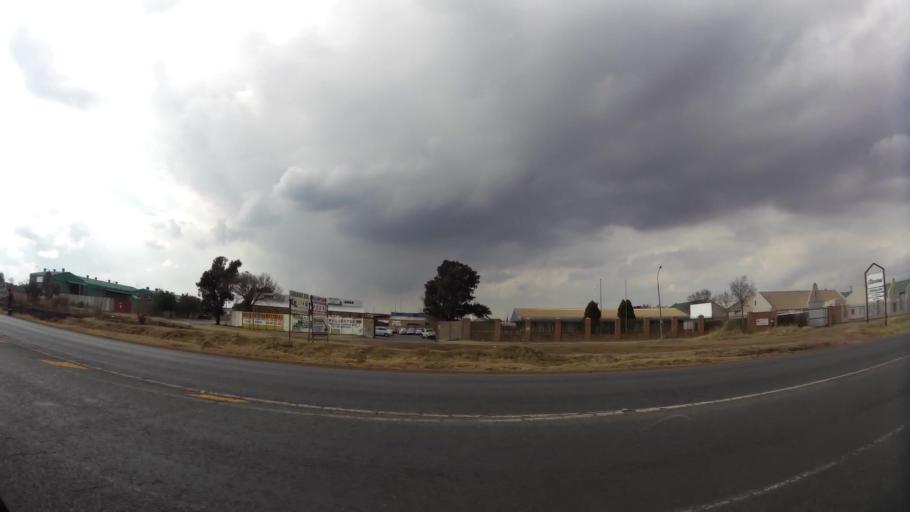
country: ZA
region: Gauteng
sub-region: Sedibeng District Municipality
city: Vanderbijlpark
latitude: -26.6781
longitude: 27.7940
